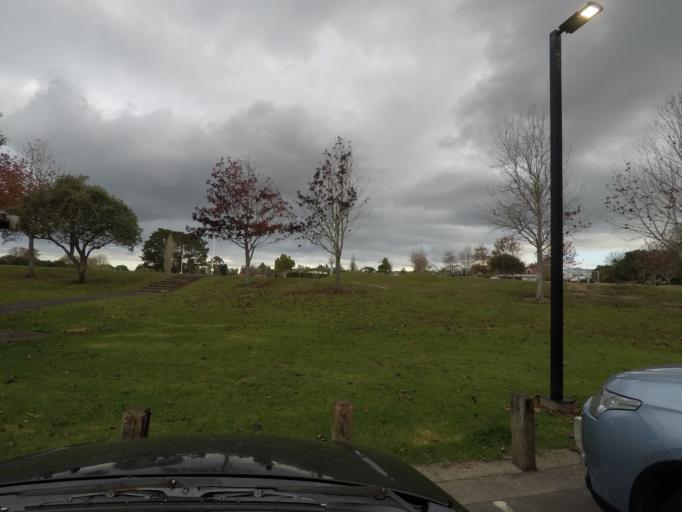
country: NZ
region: Auckland
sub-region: Auckland
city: Rosebank
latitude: -36.8283
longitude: 174.6304
